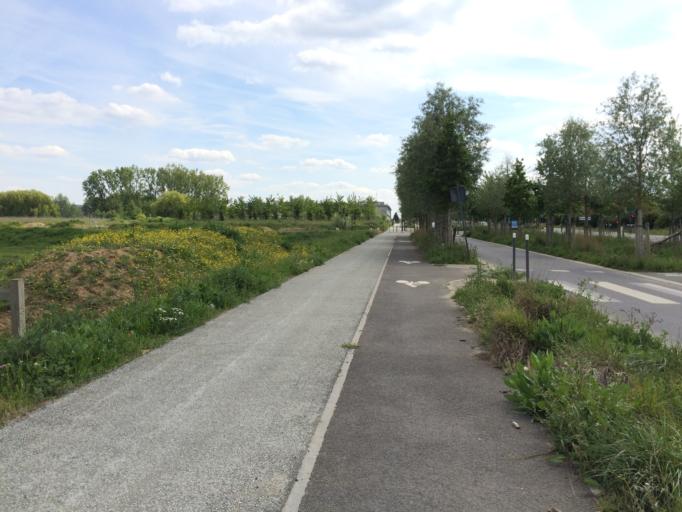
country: FR
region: Ile-de-France
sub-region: Departement de l'Essonne
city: Vauhallan
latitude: 48.7189
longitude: 2.2035
